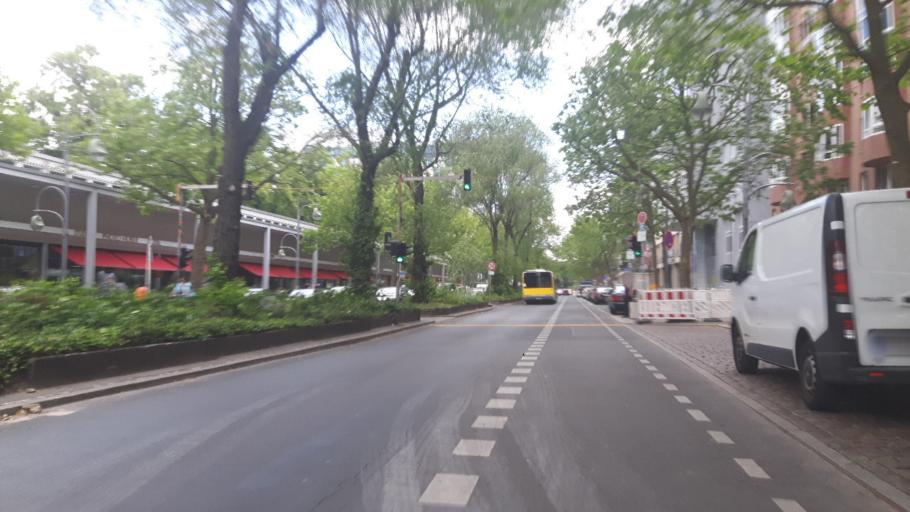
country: DE
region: Berlin
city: Hansaviertel
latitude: 52.5060
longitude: 13.3420
